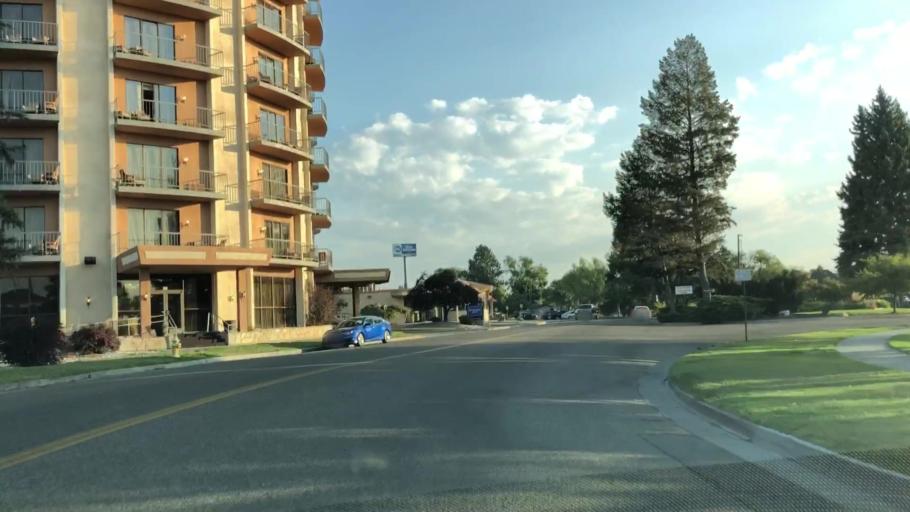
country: US
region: Idaho
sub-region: Bonneville County
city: Idaho Falls
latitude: 43.4958
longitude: -112.0448
